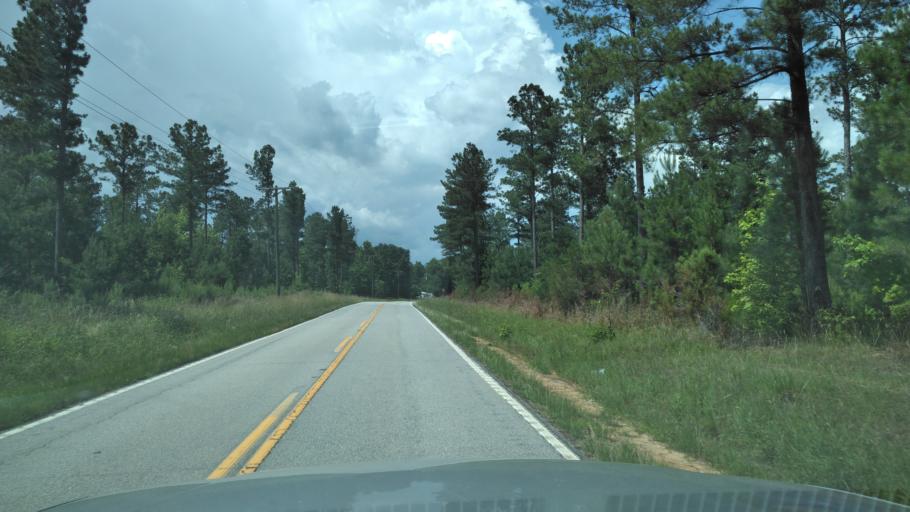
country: US
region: South Carolina
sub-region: Laurens County
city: Laurens
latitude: 34.5249
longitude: -82.0933
